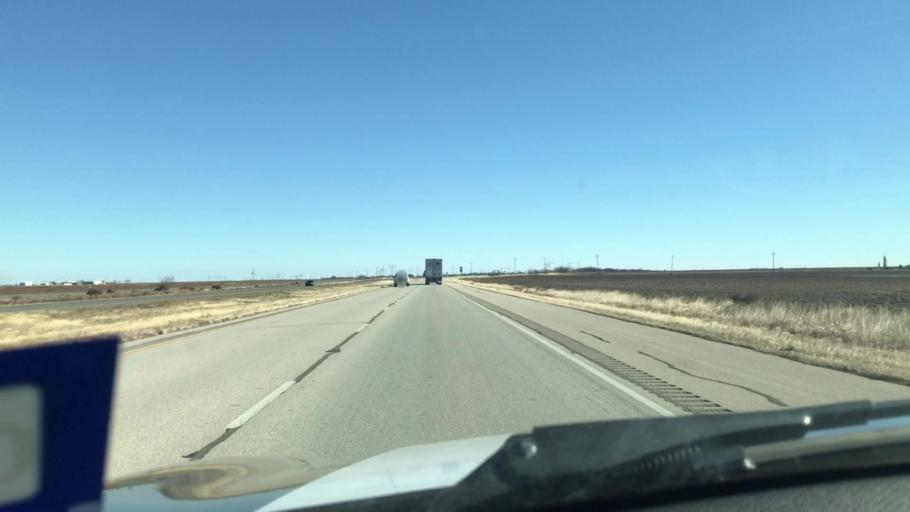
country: US
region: Texas
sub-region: Scurry County
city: Snyder
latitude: 32.6574
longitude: -100.7831
